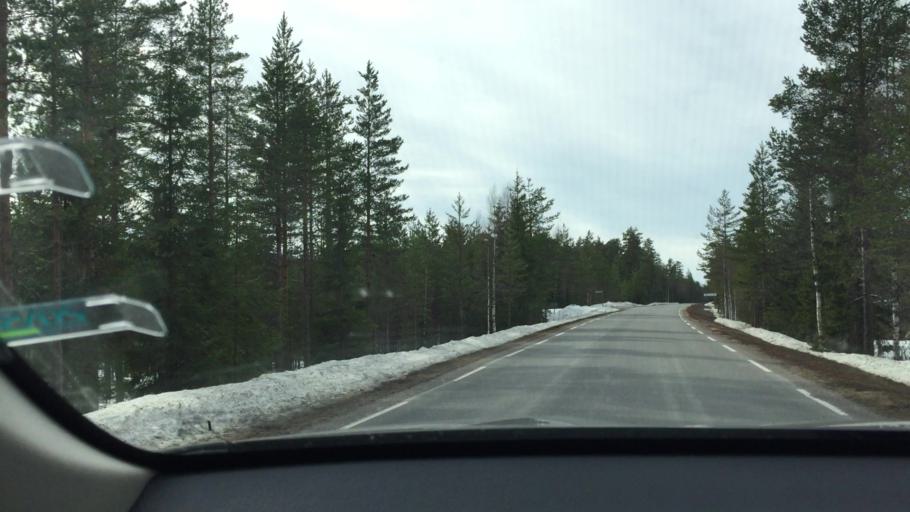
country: NO
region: Hedmark
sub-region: Trysil
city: Innbygda
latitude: 61.0642
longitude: 12.5946
